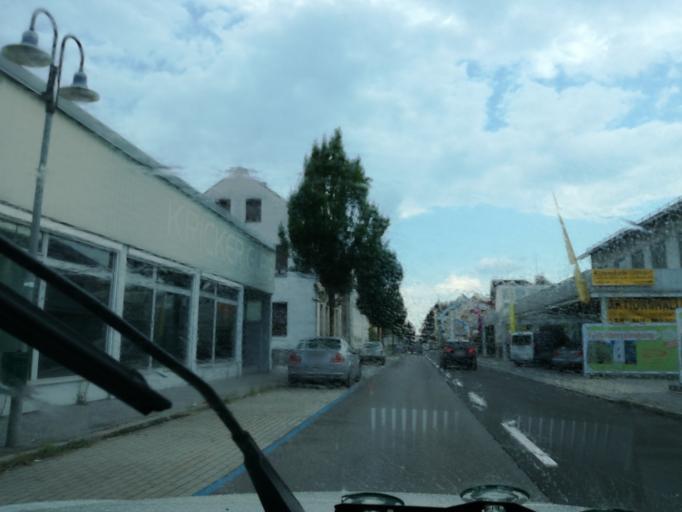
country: AT
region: Styria
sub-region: Politischer Bezirk Weiz
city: Gleisdorf
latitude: 47.1033
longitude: 15.7054
